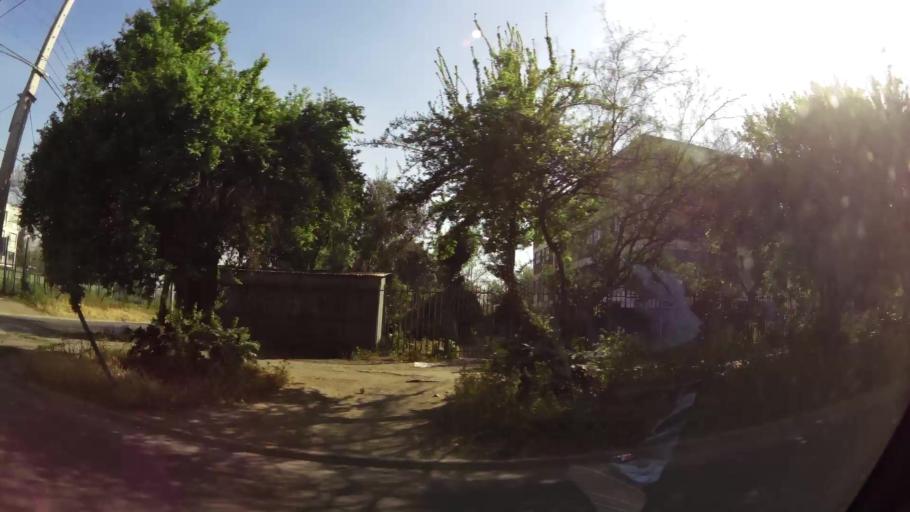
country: CL
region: Santiago Metropolitan
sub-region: Provincia de Santiago
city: Lo Prado
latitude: -33.4143
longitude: -70.7560
